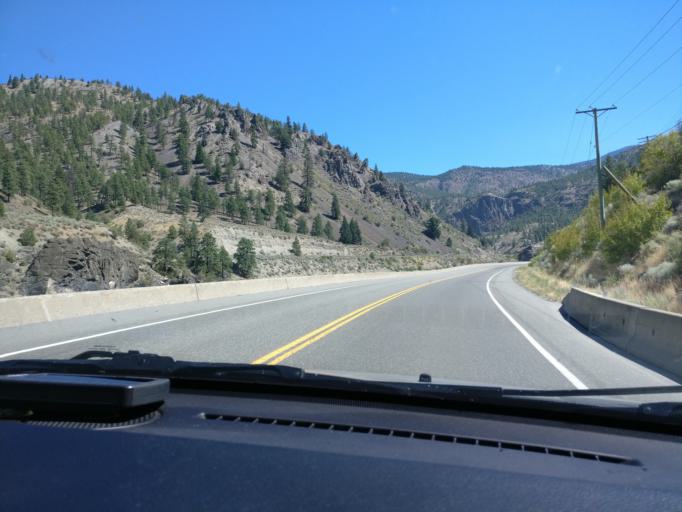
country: CA
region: British Columbia
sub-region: Thompson-Nicola Regional District
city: Ashcroft
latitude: 50.2626
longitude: -121.4175
